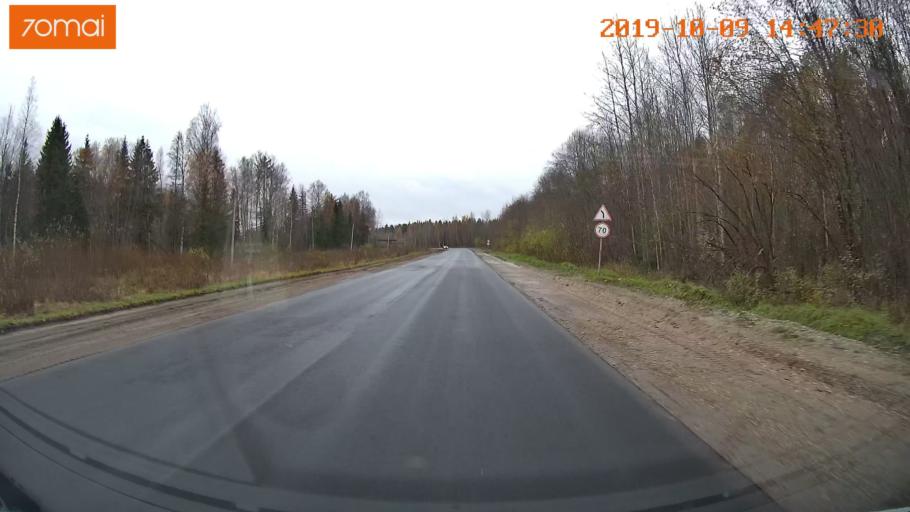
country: RU
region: Kostroma
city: Buy
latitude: 58.4172
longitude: 41.5723
